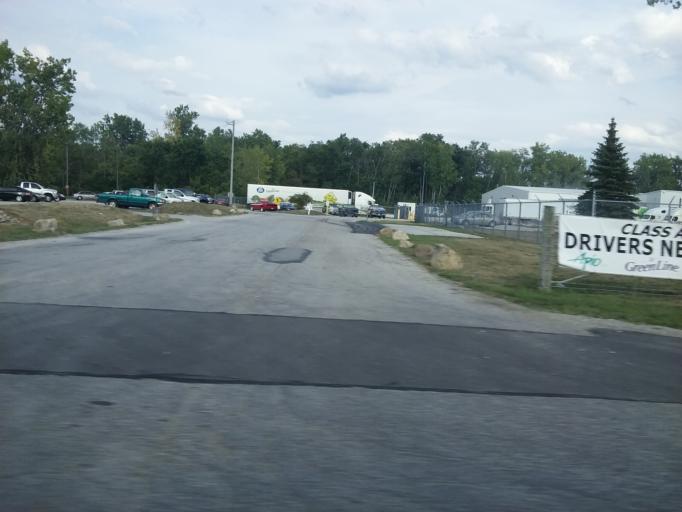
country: US
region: Ohio
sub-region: Wood County
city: Bowling Green
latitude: 41.3366
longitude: -83.6502
